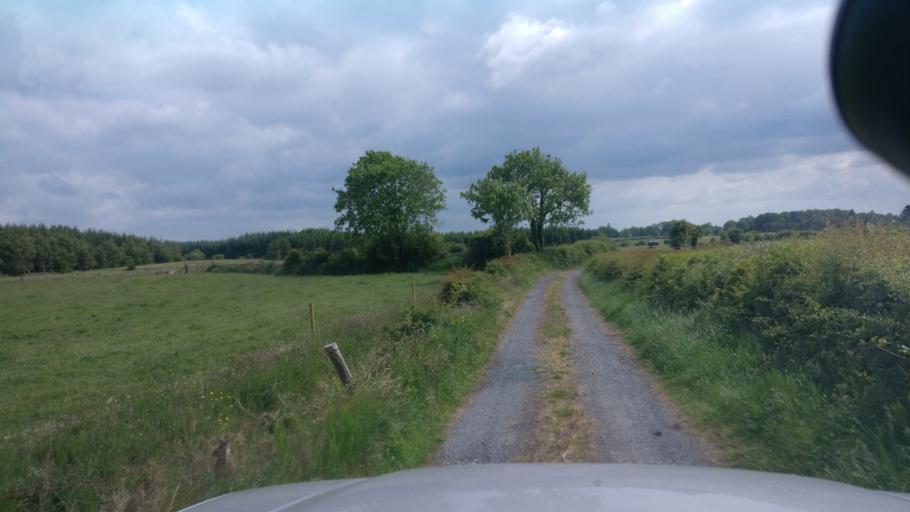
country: IE
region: Connaught
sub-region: County Galway
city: Ballinasloe
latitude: 53.2678
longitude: -8.3311
